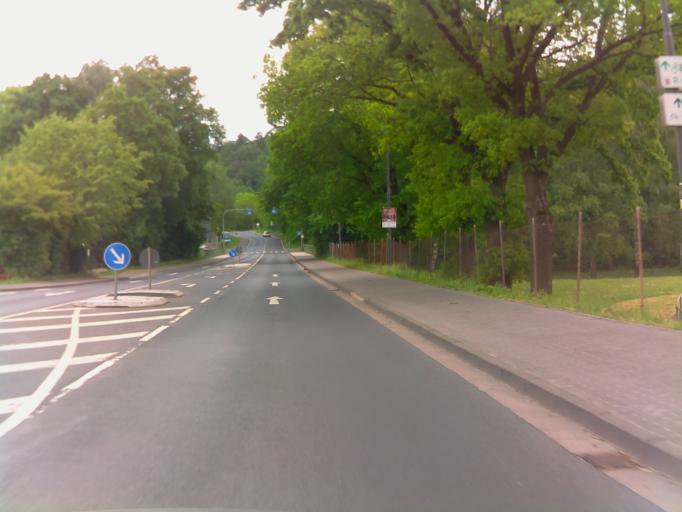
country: DE
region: Hesse
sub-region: Regierungsbezirk Giessen
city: Homberg
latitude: 50.7238
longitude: 9.0032
